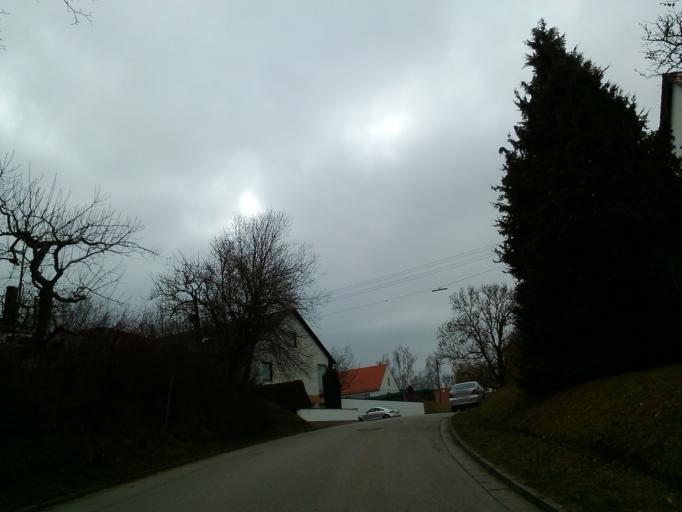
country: DE
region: Bavaria
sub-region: Swabia
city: Ustersbach
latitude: 48.3185
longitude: 10.6744
